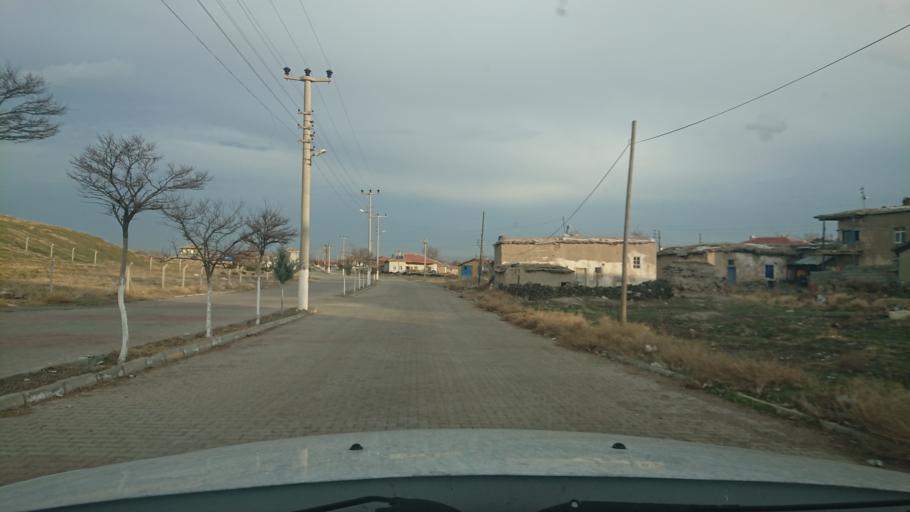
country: TR
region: Aksaray
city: Yesilova
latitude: 38.4116
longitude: 33.8390
